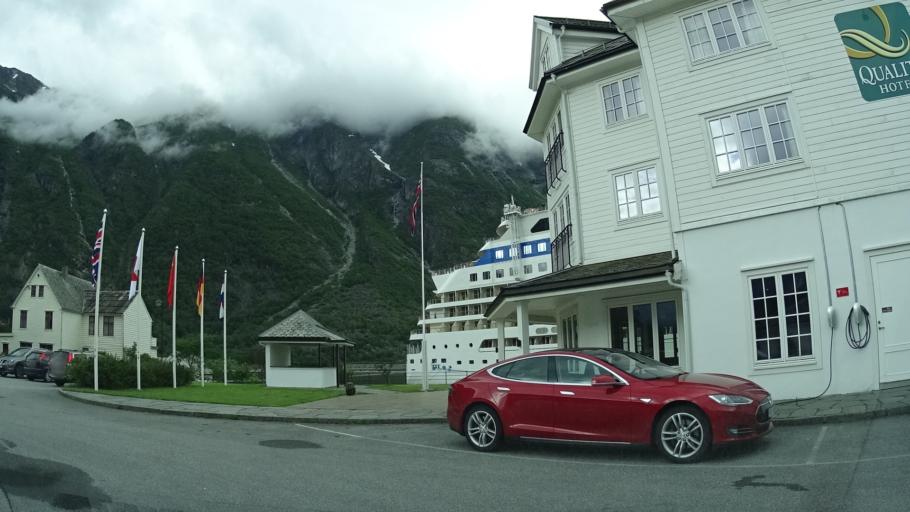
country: NO
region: Hordaland
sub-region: Eidfjord
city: Eidfjord
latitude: 60.4678
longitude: 7.0680
